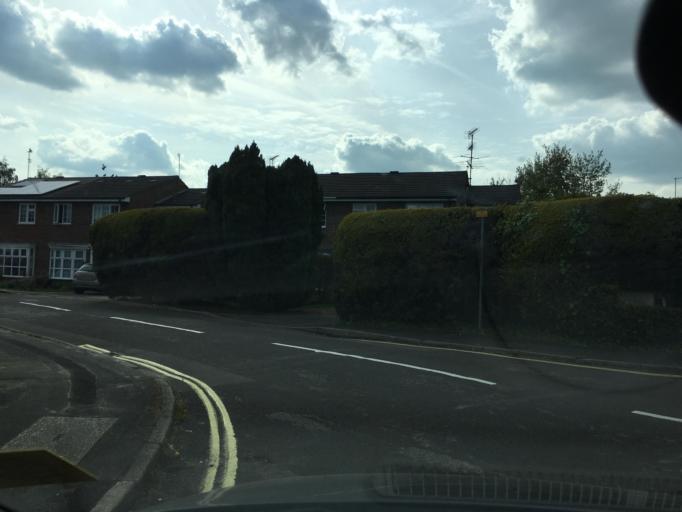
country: GB
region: England
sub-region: Hampshire
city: Farnborough
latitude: 51.2962
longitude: -0.7784
